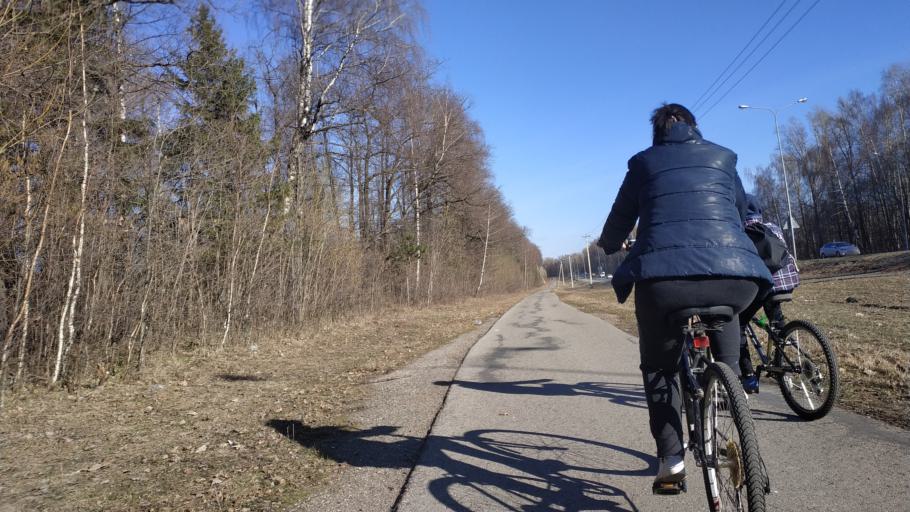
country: RU
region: Chuvashia
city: Novyye Lapsary
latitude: 56.1325
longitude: 47.1102
